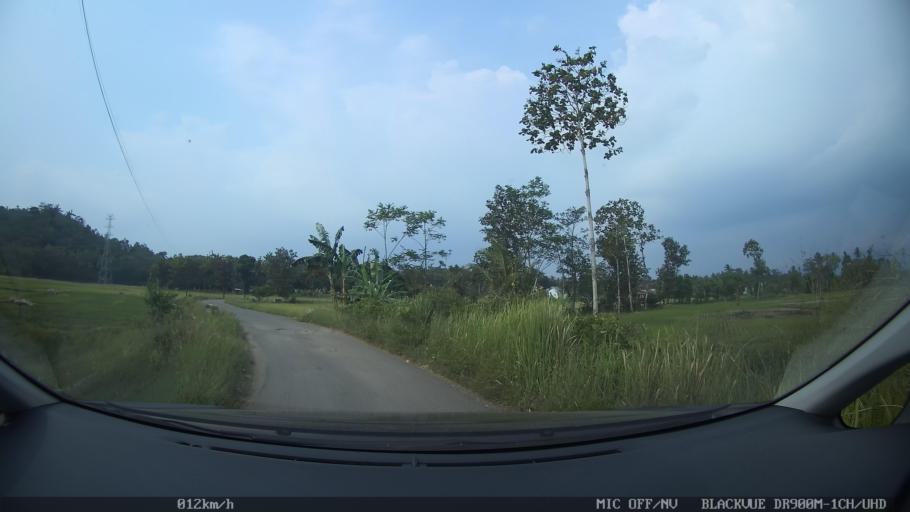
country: ID
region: Lampung
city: Gadingrejo
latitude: -5.4067
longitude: 105.0193
